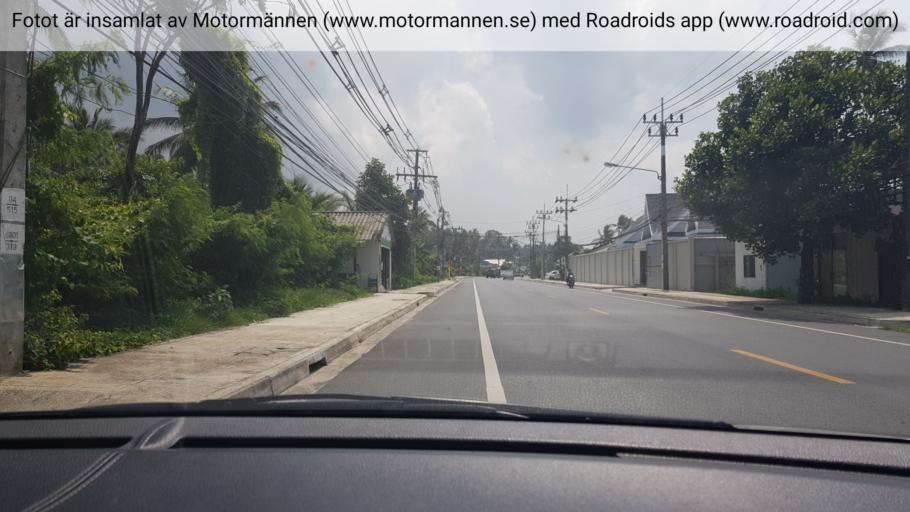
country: TH
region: Surat Thani
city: Ko Samui
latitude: 9.5534
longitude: 99.9295
